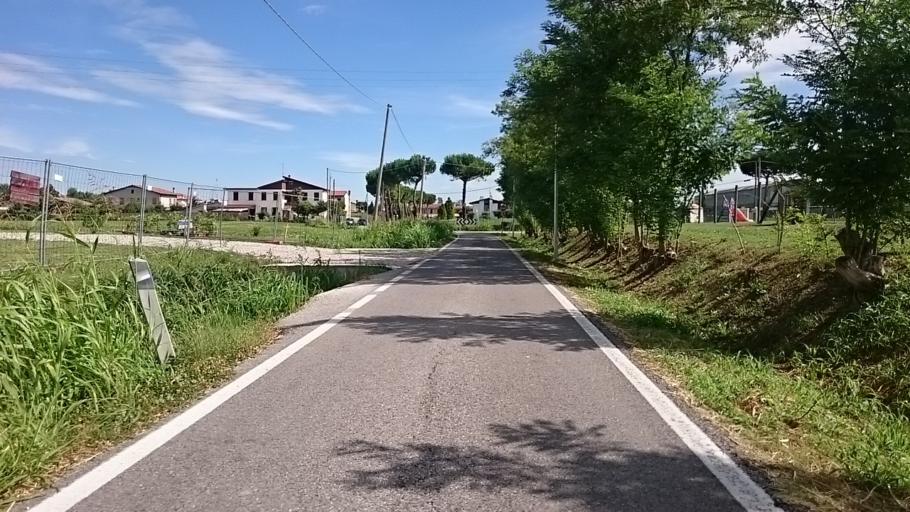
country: IT
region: Veneto
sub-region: Provincia di Padova
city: Albignasego
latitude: 45.3367
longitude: 11.8894
